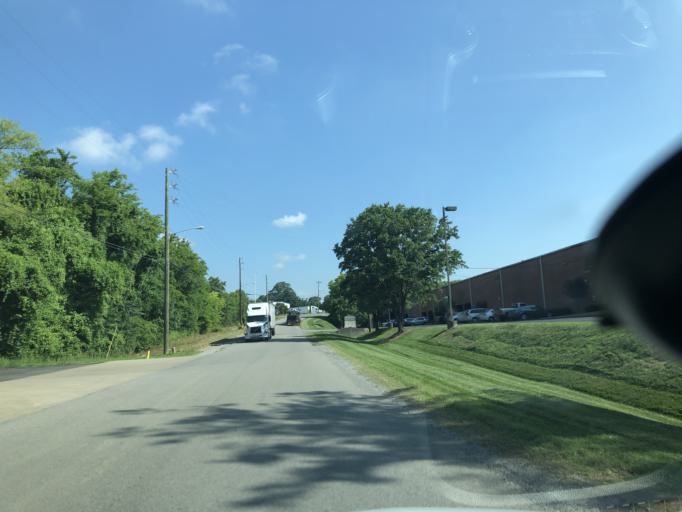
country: US
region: Tennessee
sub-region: Rutherford County
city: La Vergne
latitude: 36.0136
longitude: -86.6157
